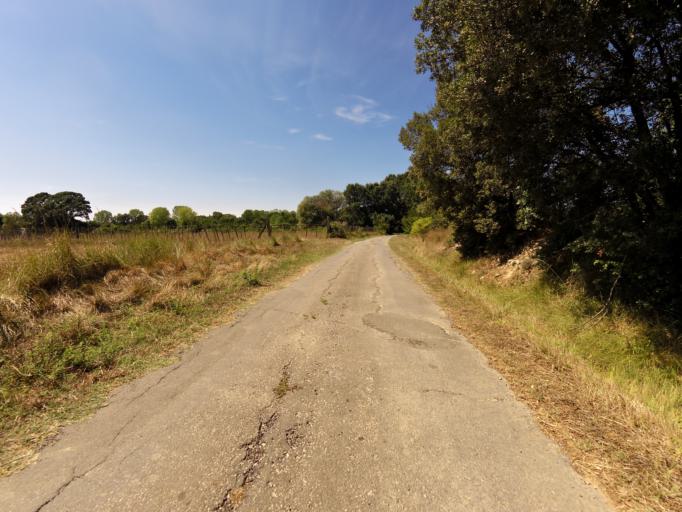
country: FR
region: Languedoc-Roussillon
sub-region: Departement du Gard
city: Aubais
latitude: 43.7564
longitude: 4.1188
